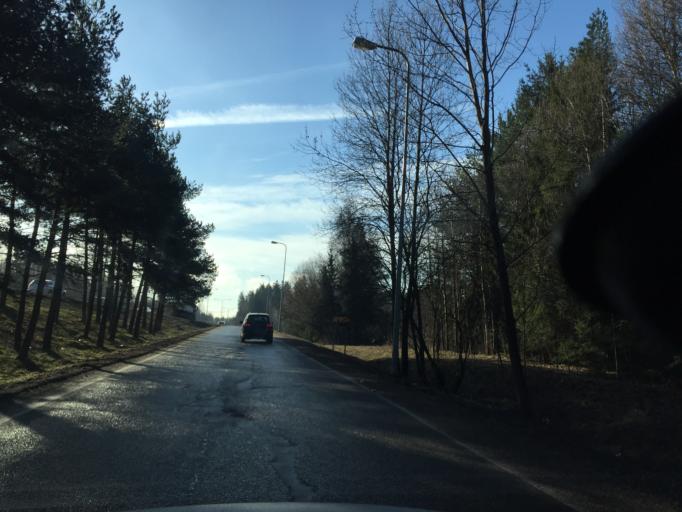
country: FI
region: Uusimaa
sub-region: Helsinki
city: Teekkarikylae
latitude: 60.2772
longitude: 24.8686
